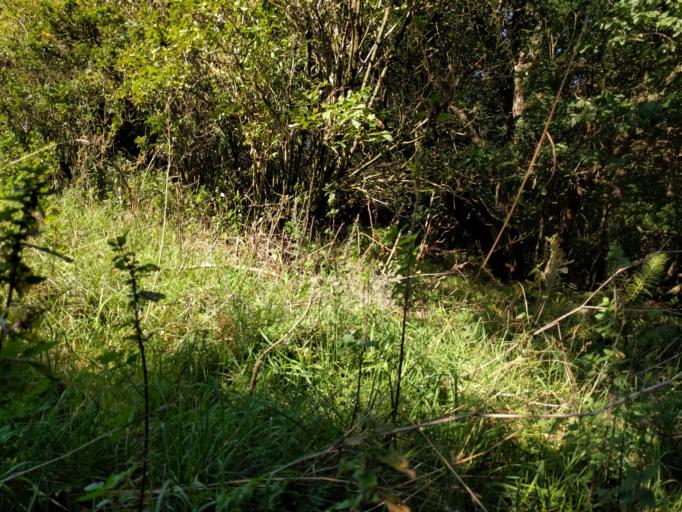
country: DK
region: Central Jutland
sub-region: Skive Kommune
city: Hojslev
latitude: 56.6679
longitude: 9.0921
